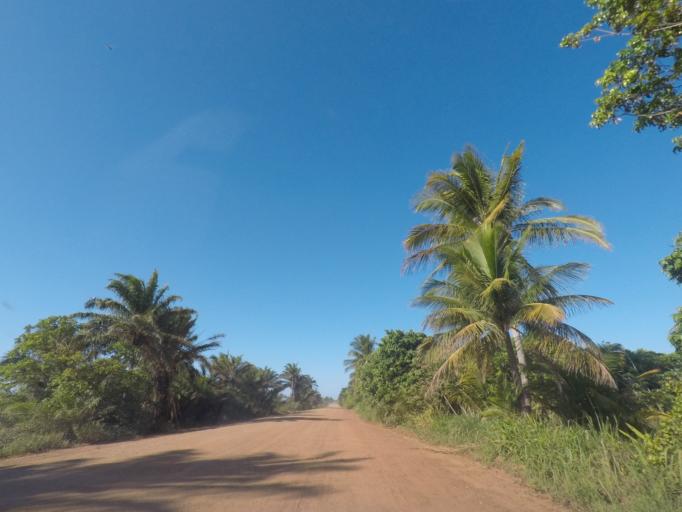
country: BR
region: Bahia
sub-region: Marau
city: Marau
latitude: -14.0590
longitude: -38.9569
